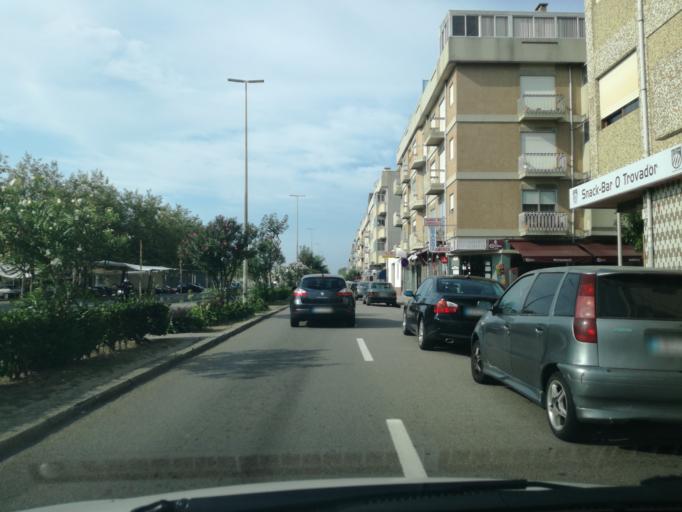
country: PT
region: Aveiro
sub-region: Espinho
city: Espinho
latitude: 41.0045
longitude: -8.6381
